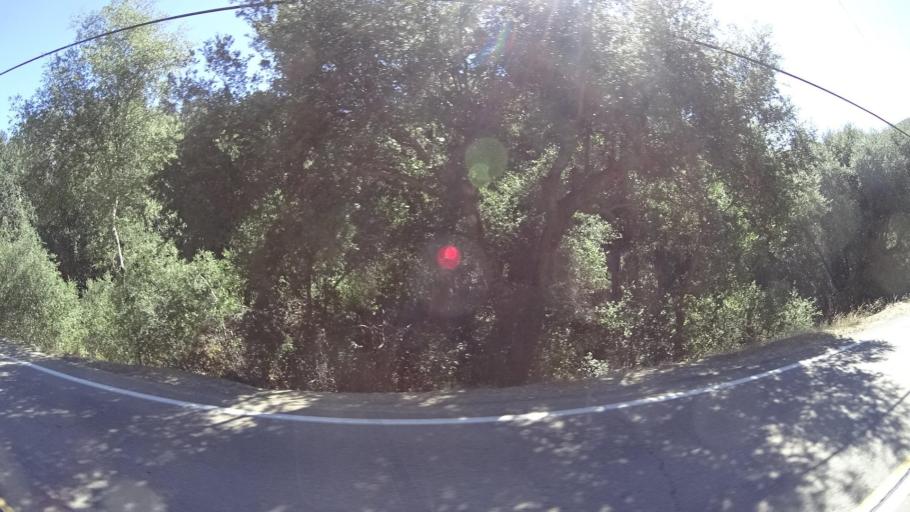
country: US
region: California
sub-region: San Diego County
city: Descanso
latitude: 32.8157
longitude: -116.6308
